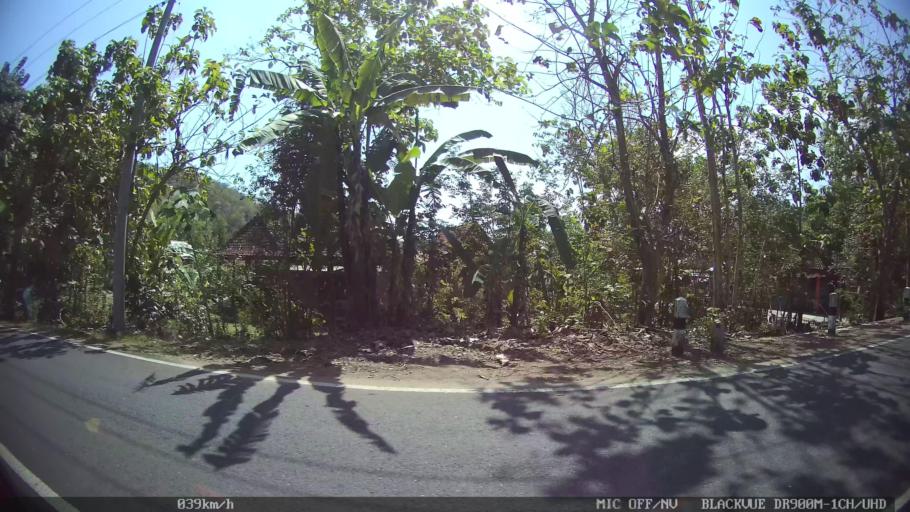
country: ID
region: Daerah Istimewa Yogyakarta
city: Pundong
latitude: -7.9595
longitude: 110.3778
